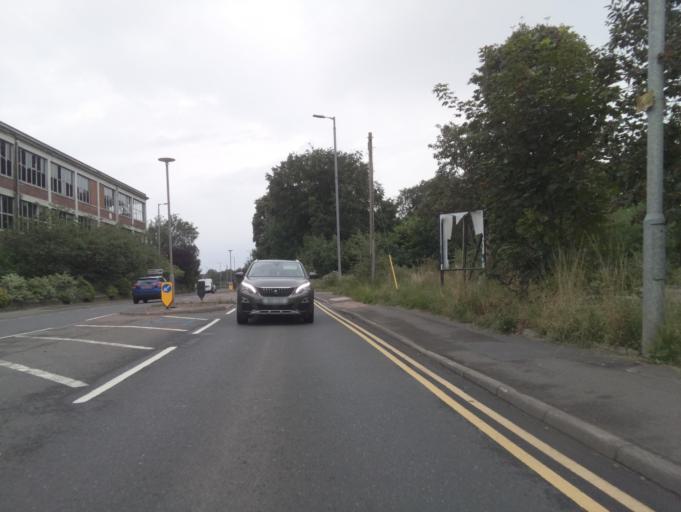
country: GB
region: Scotland
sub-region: Dumfries and Galloway
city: Locharbriggs
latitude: 55.0962
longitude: -3.5865
